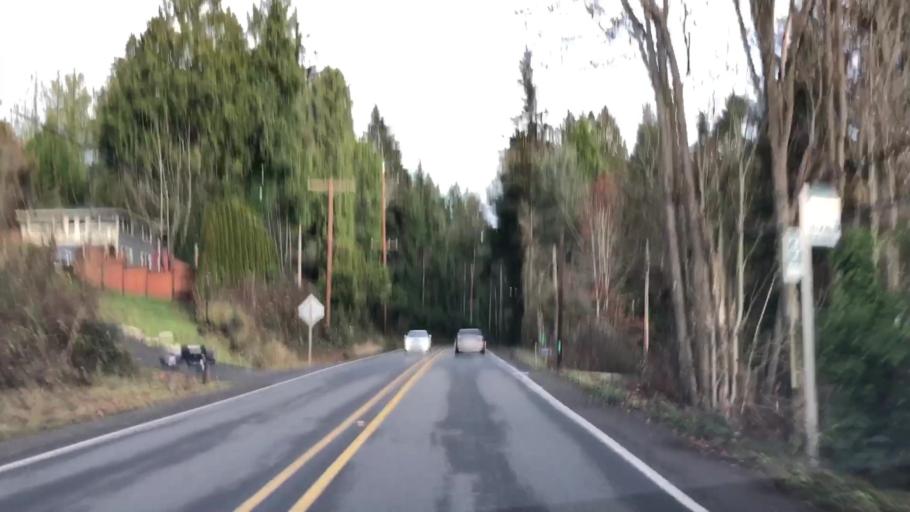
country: US
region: Washington
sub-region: Kitsap County
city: Suquamish
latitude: 47.7512
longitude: -122.5627
